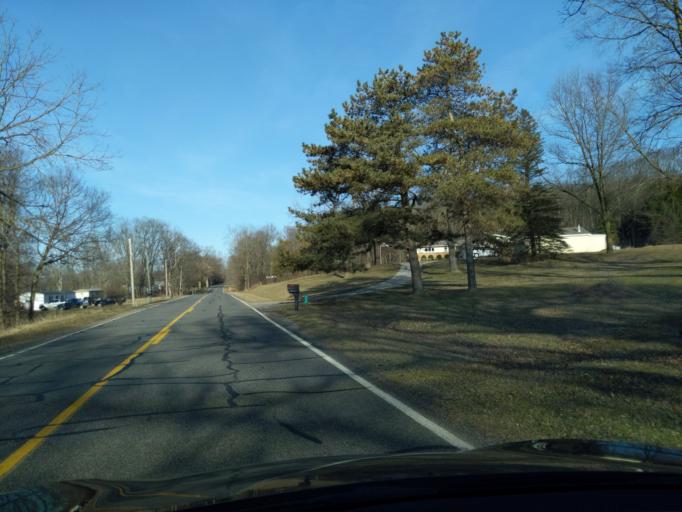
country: US
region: Michigan
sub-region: Ionia County
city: Saranac
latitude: 42.9391
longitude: -85.1829
